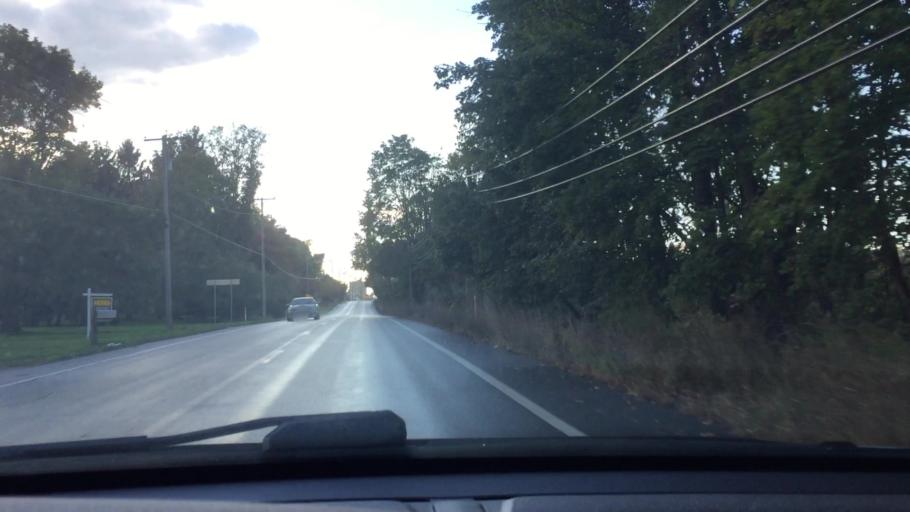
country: US
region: Pennsylvania
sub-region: Lawrence County
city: Bessemer
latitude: 40.9761
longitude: -80.4648
